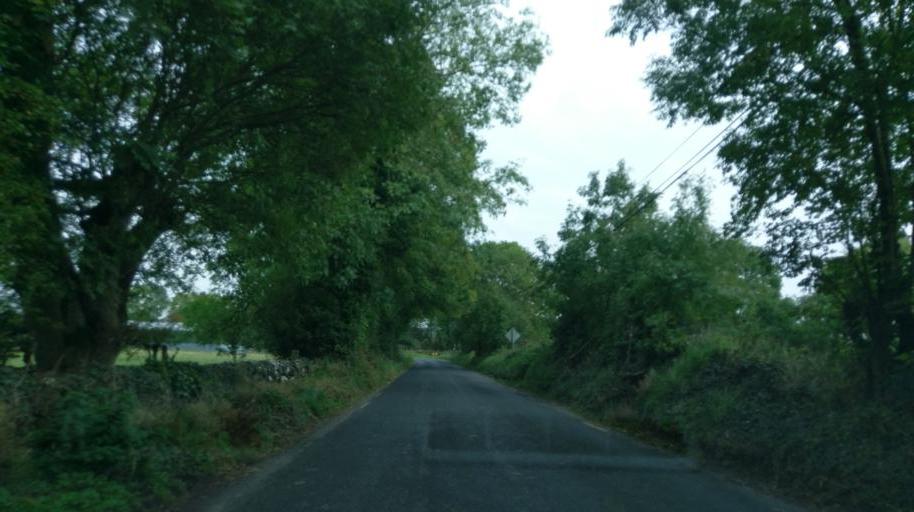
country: IE
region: Connaught
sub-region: County Galway
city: Athenry
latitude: 53.3659
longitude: -8.7006
